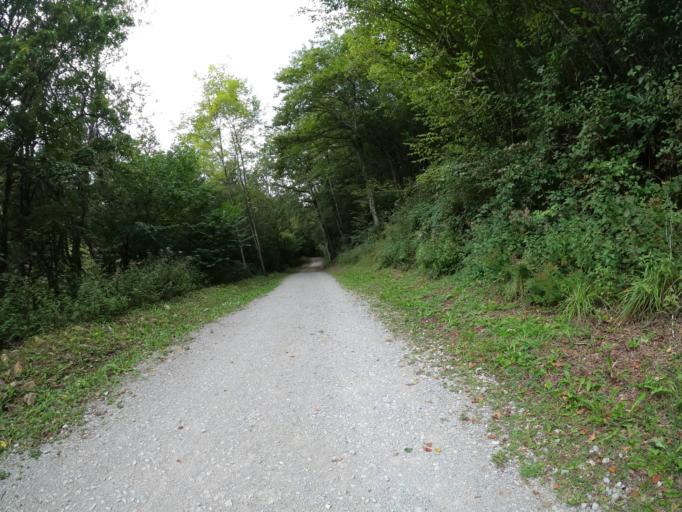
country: ES
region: Navarre
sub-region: Provincia de Navarra
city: Lekunberri
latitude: 42.9852
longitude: -1.8727
